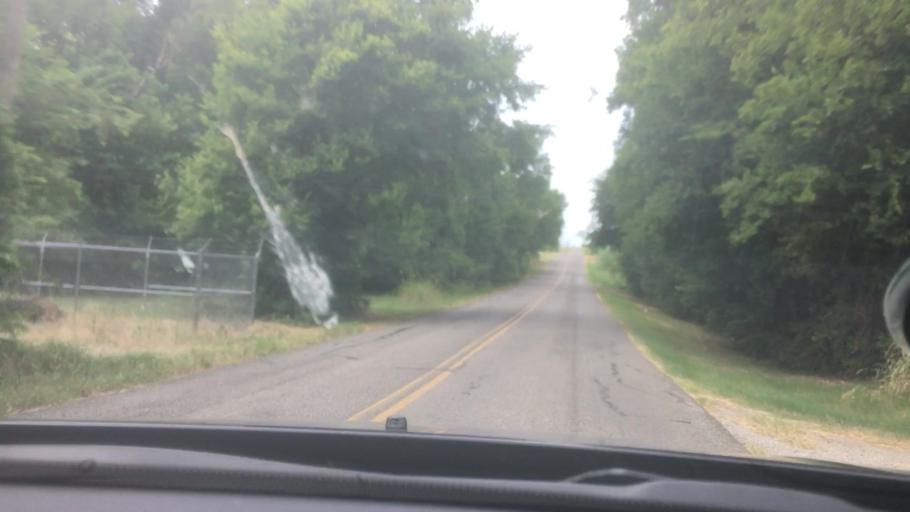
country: US
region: Oklahoma
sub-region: Murray County
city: Davis
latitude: 34.4956
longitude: -97.0554
